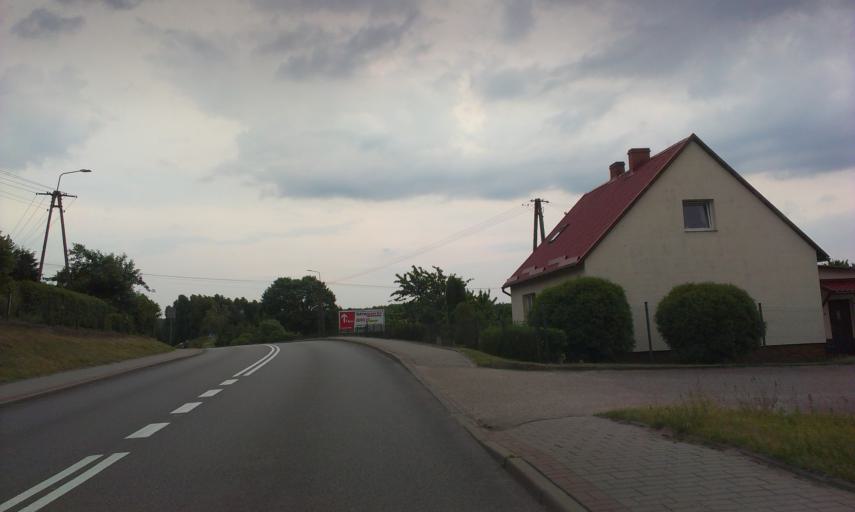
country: PL
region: West Pomeranian Voivodeship
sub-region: Powiat koszalinski
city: Bobolice
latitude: 53.8581
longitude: 16.6084
